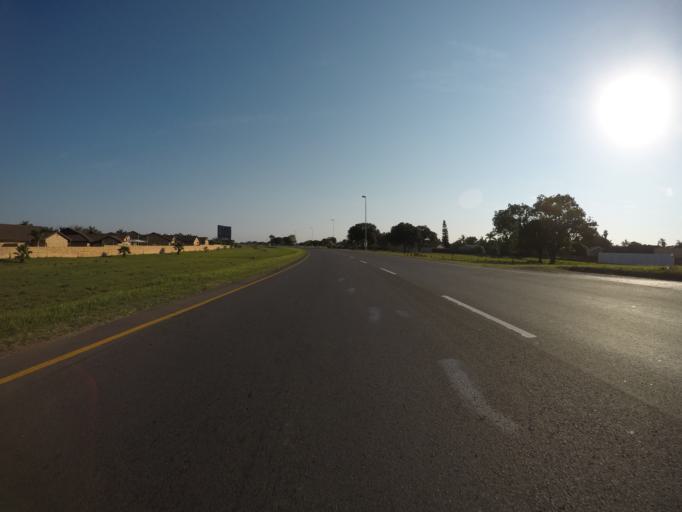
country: ZA
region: KwaZulu-Natal
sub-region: uThungulu District Municipality
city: Richards Bay
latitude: -28.7545
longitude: 32.0578
